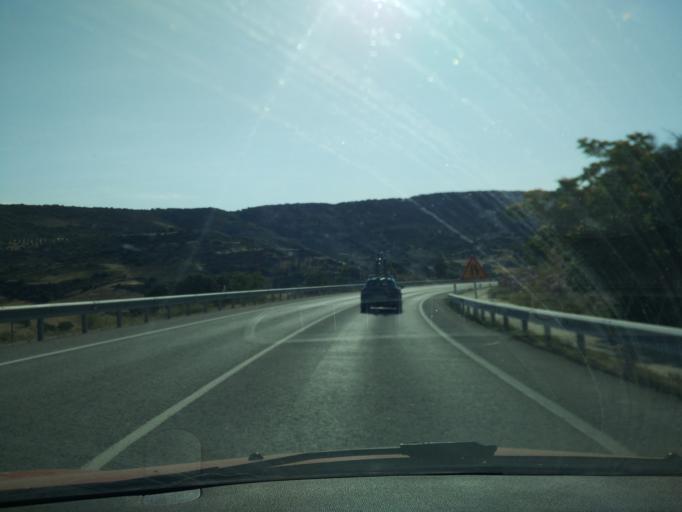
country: ES
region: Madrid
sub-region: Provincia de Madrid
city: Villar del Olmo
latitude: 40.3322
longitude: -3.2314
